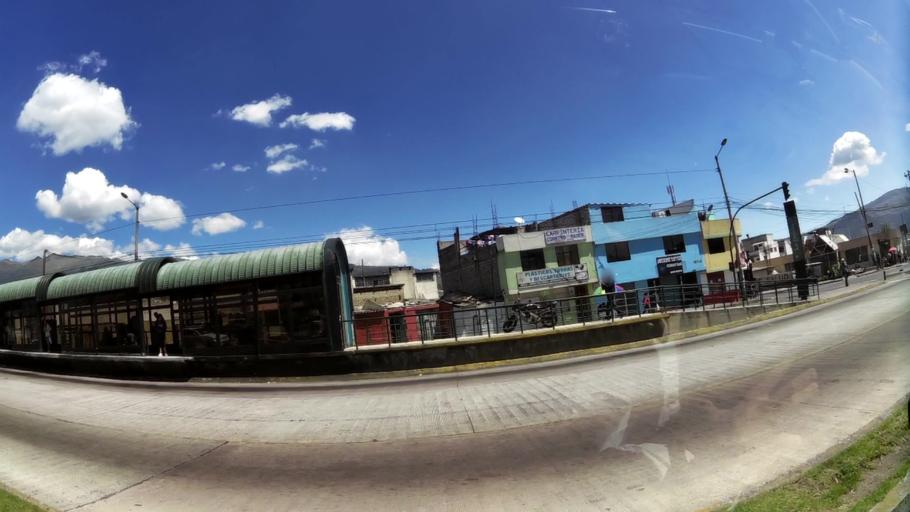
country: EC
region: Pichincha
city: Quito
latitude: -0.1157
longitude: -78.4908
